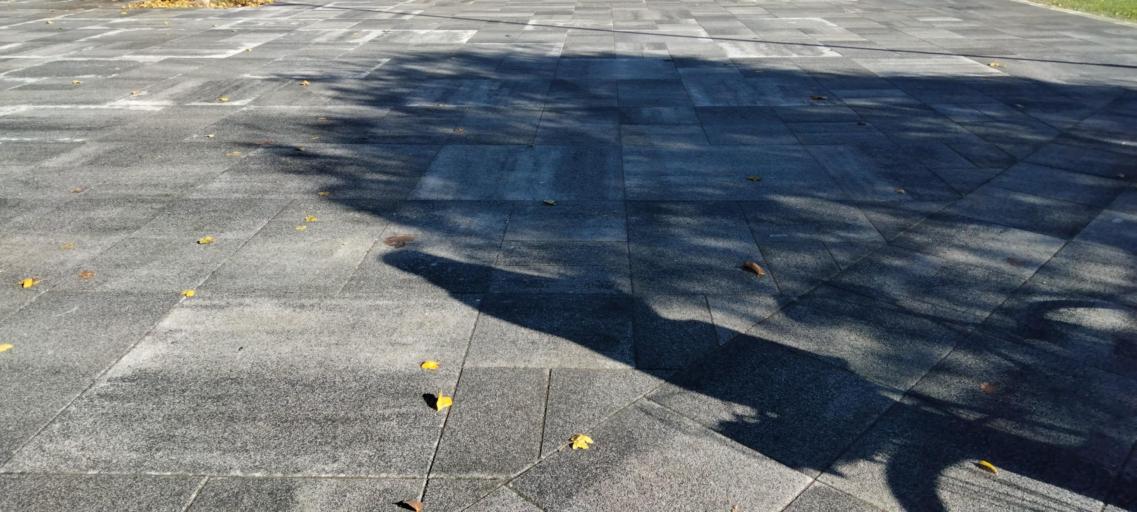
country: IT
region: Veneto
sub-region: Provincia di Vicenza
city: Creazzo
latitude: 45.5316
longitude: 11.4787
